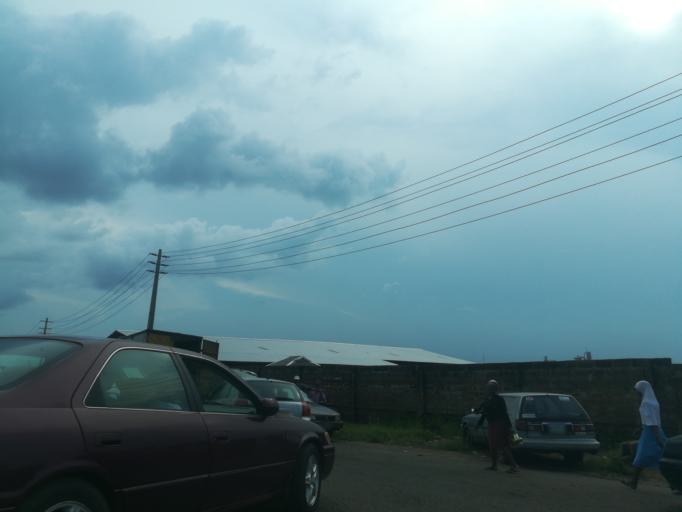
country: NG
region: Oyo
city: Ibadan
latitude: 7.3659
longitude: 3.8527
